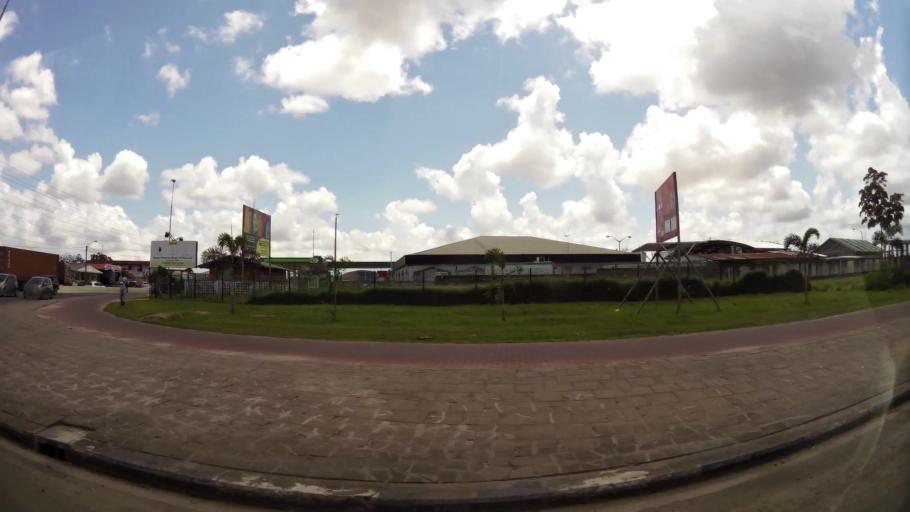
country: SR
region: Paramaribo
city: Paramaribo
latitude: 5.8066
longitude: -55.1727
